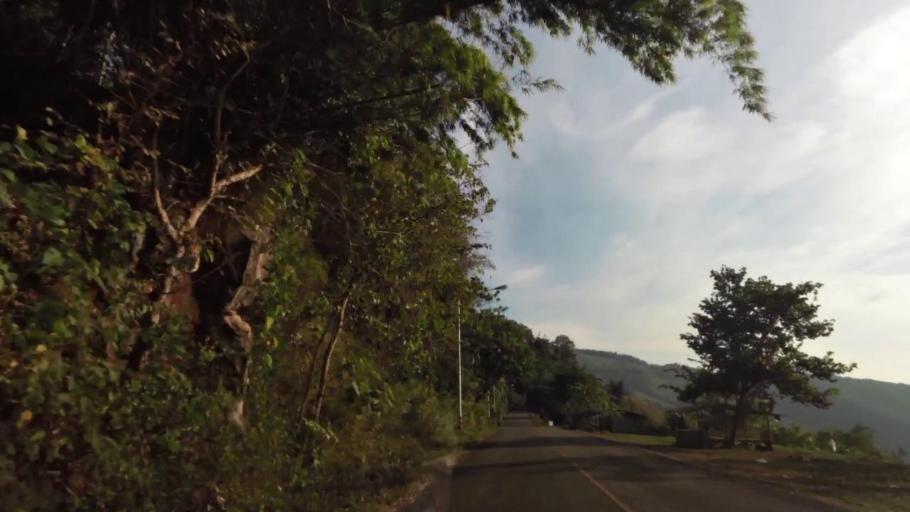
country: TH
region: Chiang Rai
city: Khun Tan
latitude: 19.8541
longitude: 100.4366
